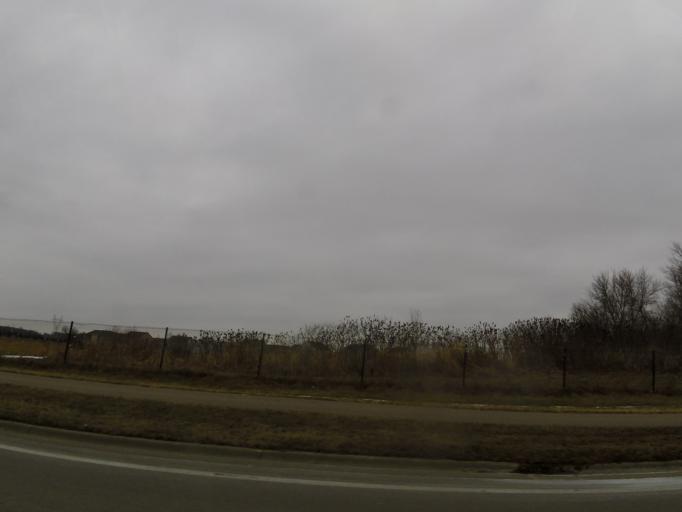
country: US
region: Minnesota
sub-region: Carver County
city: Chaska
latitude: 44.8058
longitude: -93.6288
